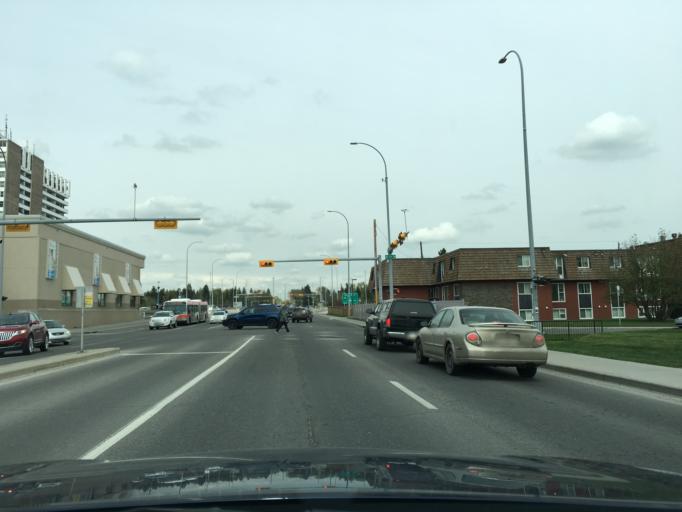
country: CA
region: Alberta
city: Calgary
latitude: 50.9921
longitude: -114.0831
